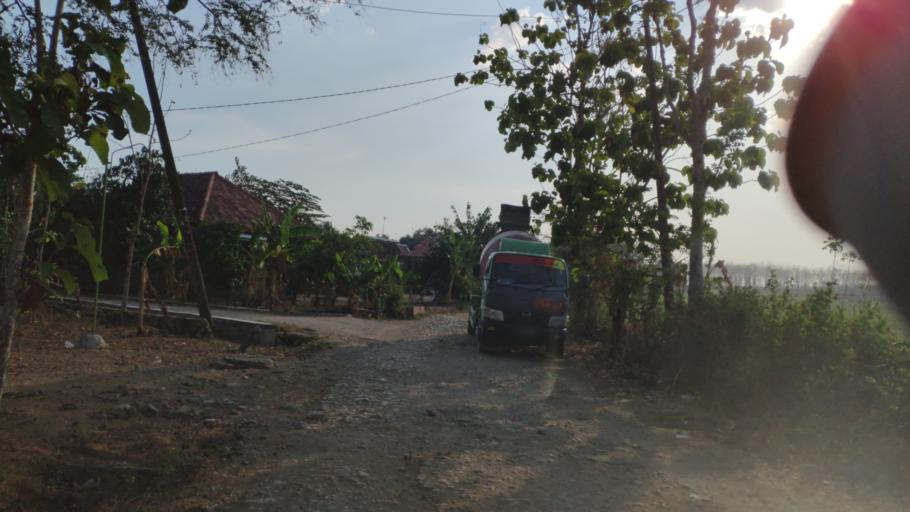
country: ID
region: Central Java
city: Pelem
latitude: -6.9941
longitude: 111.1948
